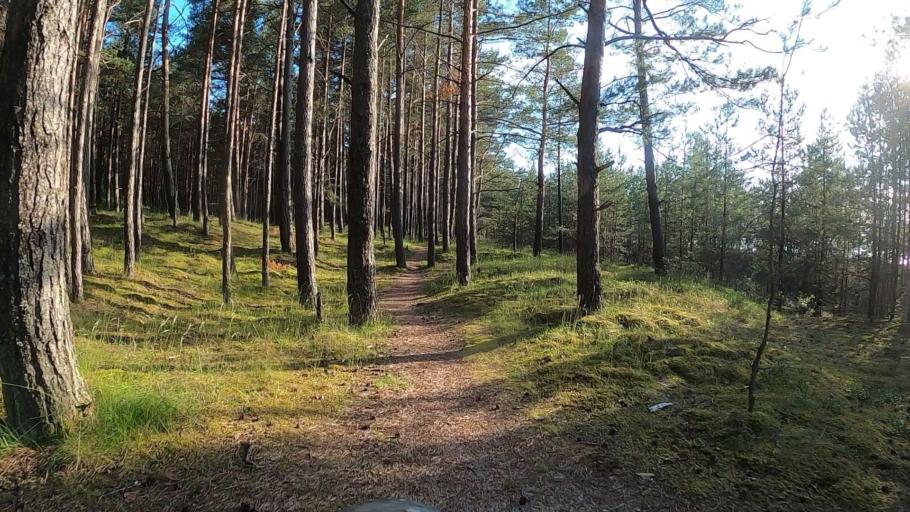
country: LV
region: Carnikava
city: Carnikava
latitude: 57.1226
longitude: 24.2090
